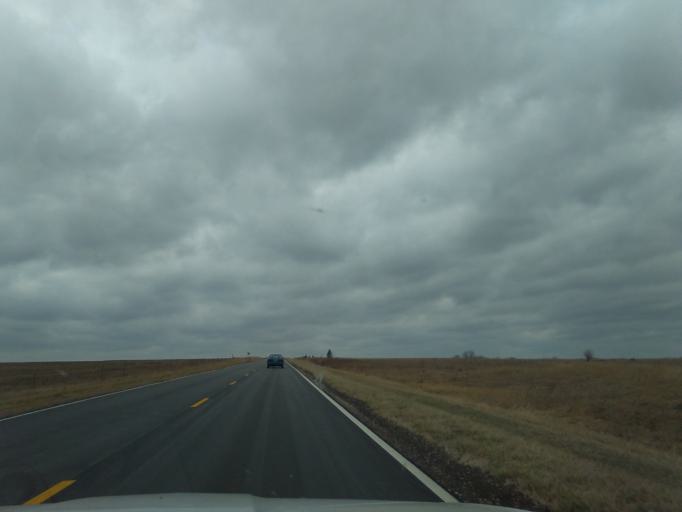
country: US
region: Nebraska
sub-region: Pawnee County
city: Pawnee City
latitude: 40.0515
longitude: -96.0125
